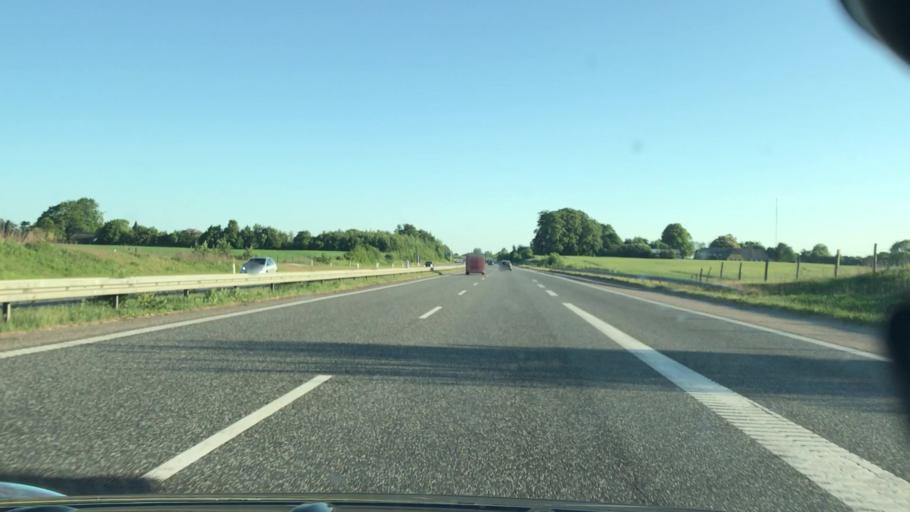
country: DK
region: South Denmark
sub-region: Faaborg-Midtfyn Kommune
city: Ringe
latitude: 55.2573
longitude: 10.4715
